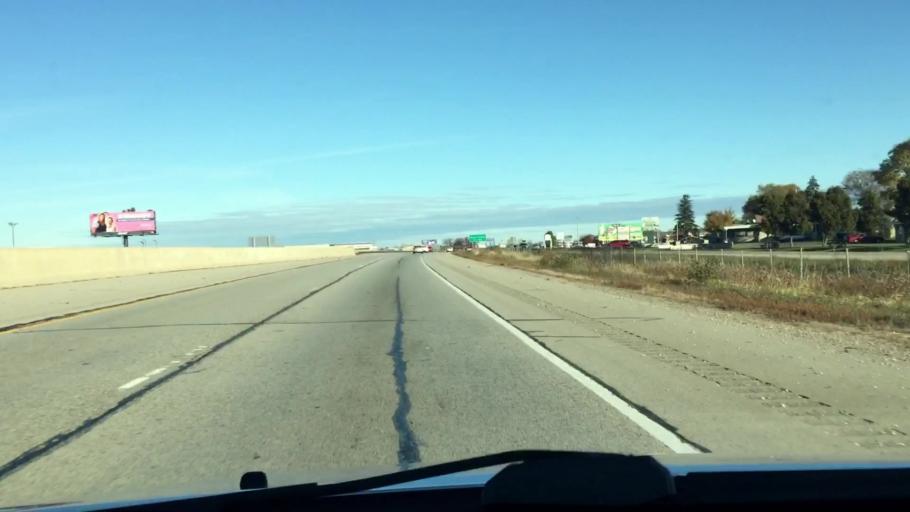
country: US
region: Wisconsin
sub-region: Fond du Lac County
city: Fond du Lac
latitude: 43.7680
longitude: -88.4811
